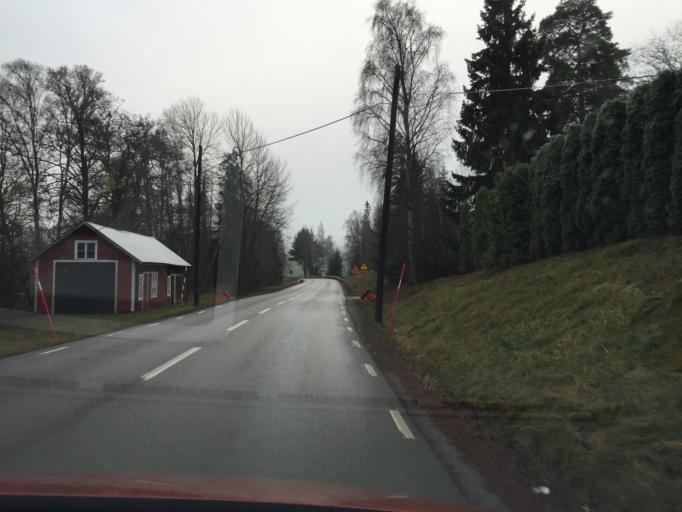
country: SE
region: Stockholm
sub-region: Botkyrka Kommun
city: Varsta
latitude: 59.1389
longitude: 17.8351
